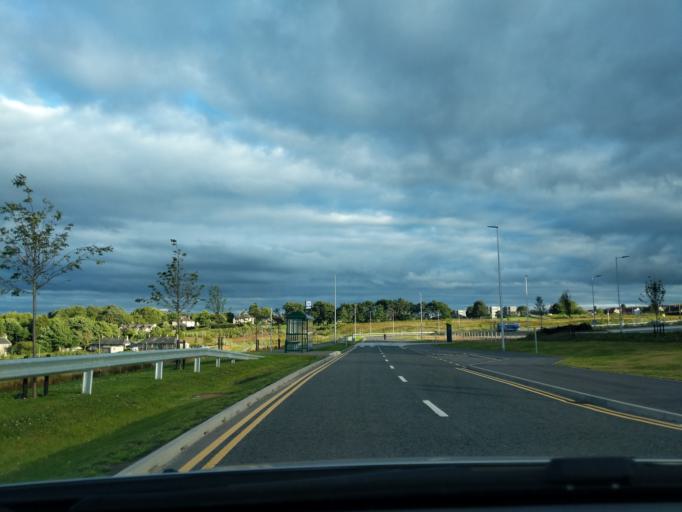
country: GB
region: Scotland
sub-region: Aberdeen City
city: Dyce
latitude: 57.1863
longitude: -2.1875
